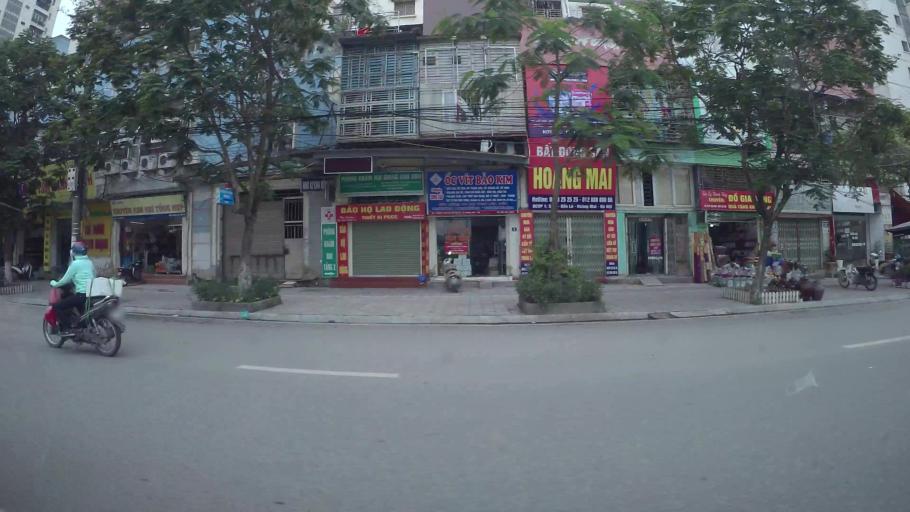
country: VN
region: Ha Noi
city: Hai BaTrung
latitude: 20.9836
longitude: 105.8584
